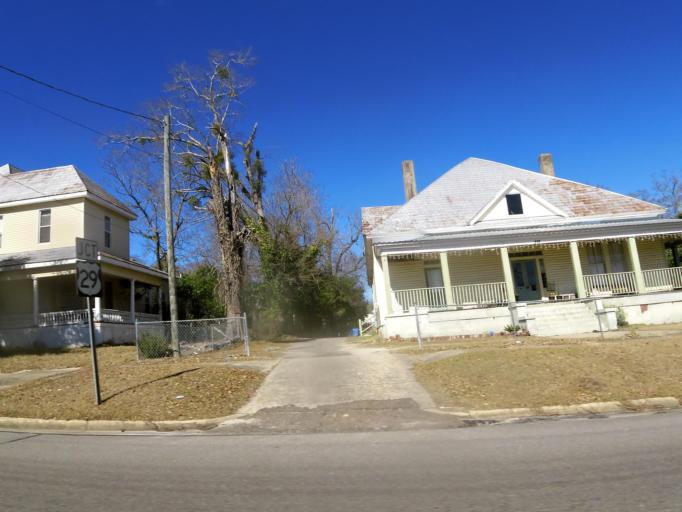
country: US
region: Alabama
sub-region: Bullock County
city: Union Springs
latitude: 32.1463
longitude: -85.7111
